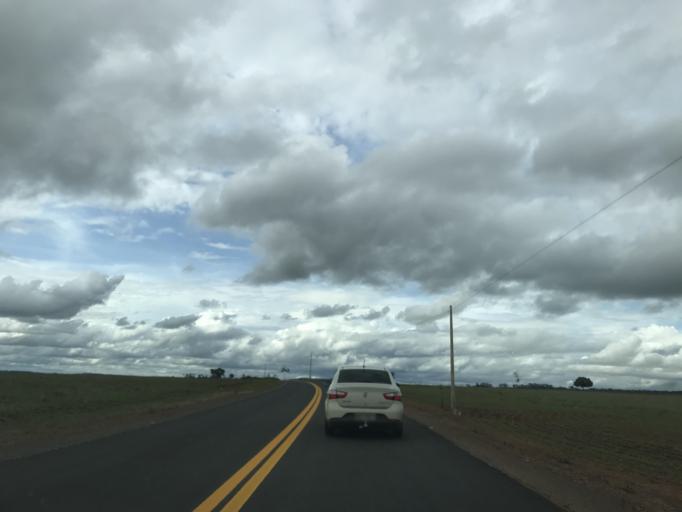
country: BR
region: Goias
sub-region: Bela Vista De Goias
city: Bela Vista de Goias
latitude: -17.0890
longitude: -48.6530
